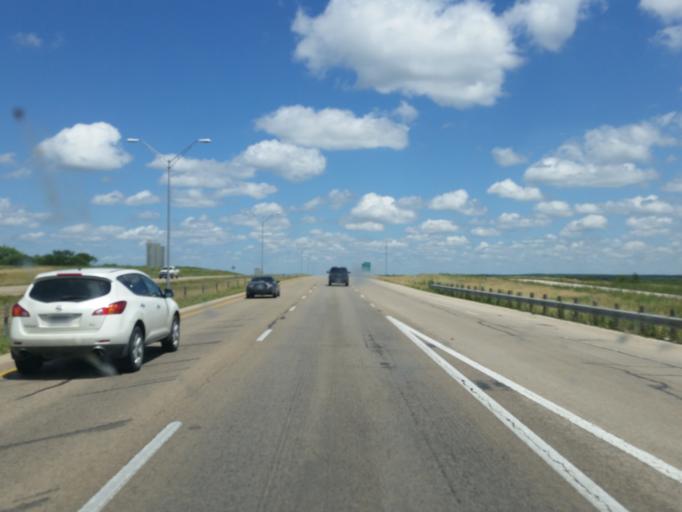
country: US
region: Texas
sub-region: Callahan County
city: Baird
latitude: 32.4004
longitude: -99.3808
